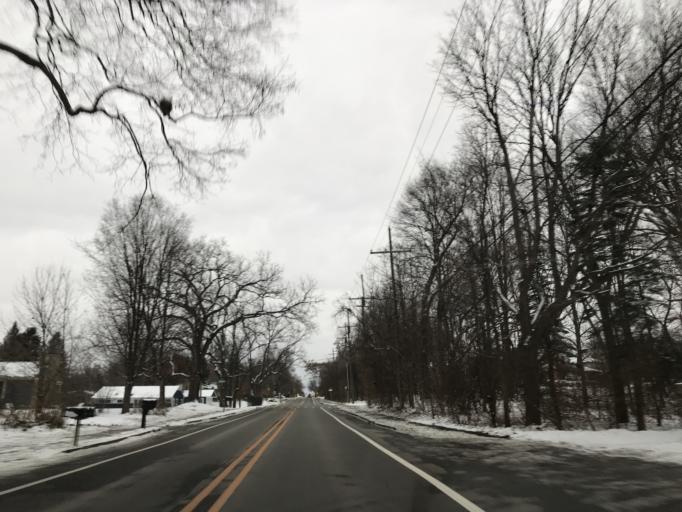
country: US
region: Michigan
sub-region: Washtenaw County
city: Ann Arbor
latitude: 42.3029
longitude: -83.7351
